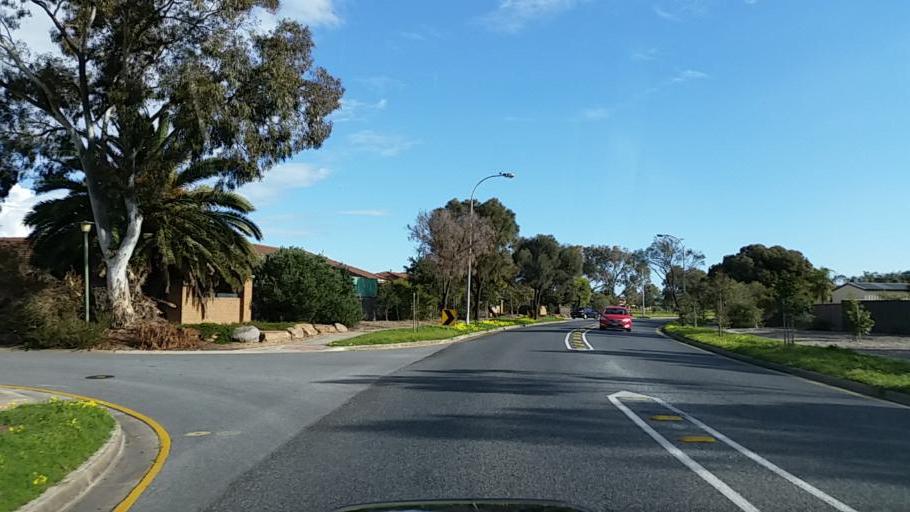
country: AU
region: South Australia
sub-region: Charles Sturt
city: West Lakes Shore
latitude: -34.8579
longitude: 138.4937
